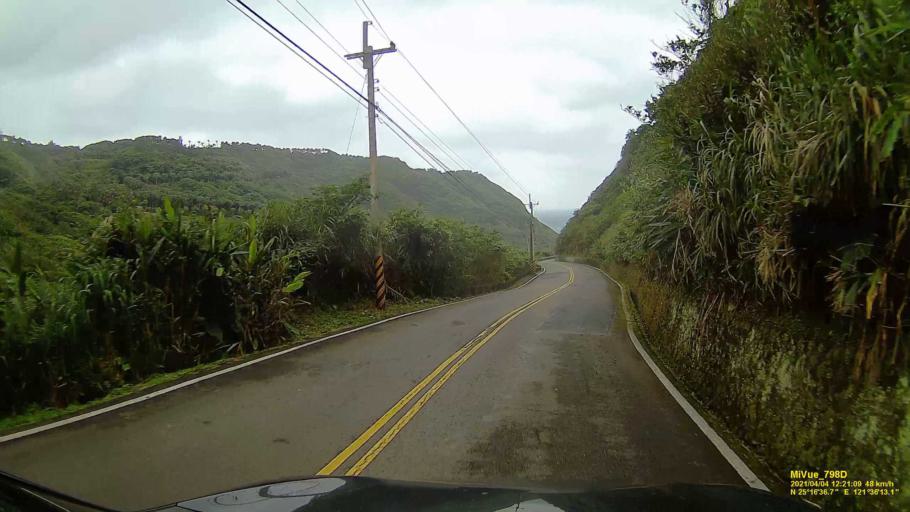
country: TW
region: Taiwan
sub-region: Keelung
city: Keelung
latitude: 25.2772
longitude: 121.6038
